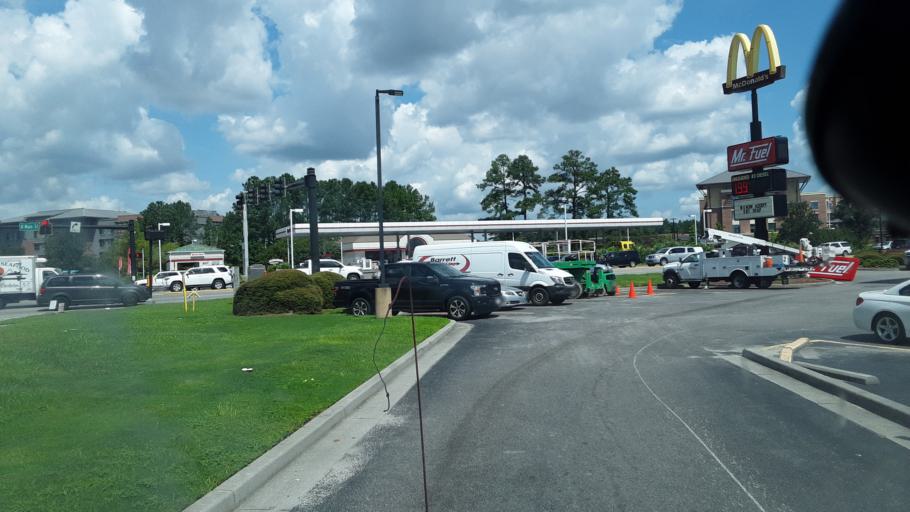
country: US
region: South Carolina
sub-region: Berkeley County
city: Sangaree
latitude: 33.0388
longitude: -80.1429
